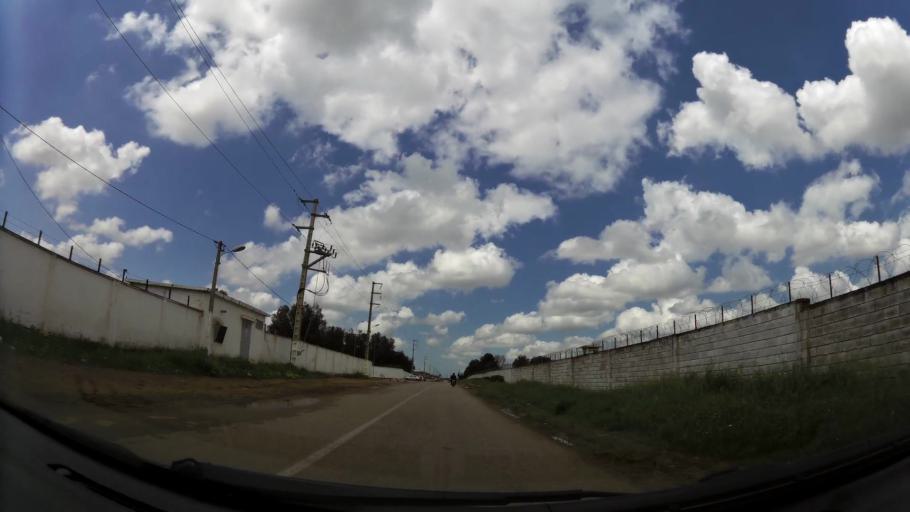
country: MA
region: Chaouia-Ouardigha
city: Nouaseur
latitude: 33.3891
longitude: -7.5770
